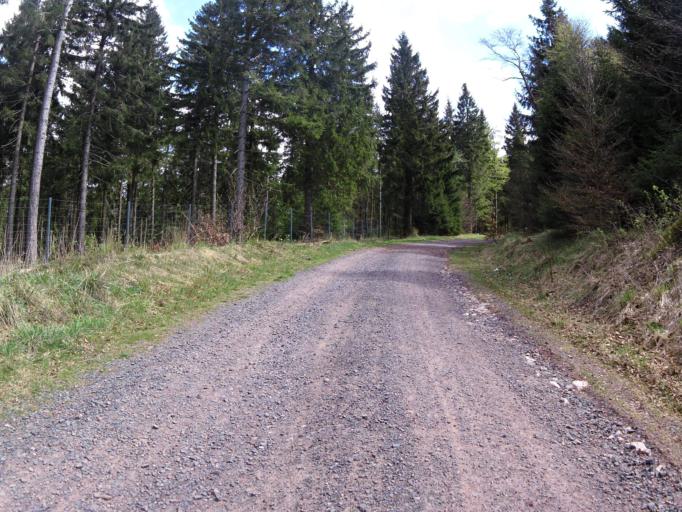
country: DE
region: Thuringia
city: Tabarz
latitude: 50.8437
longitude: 10.4873
